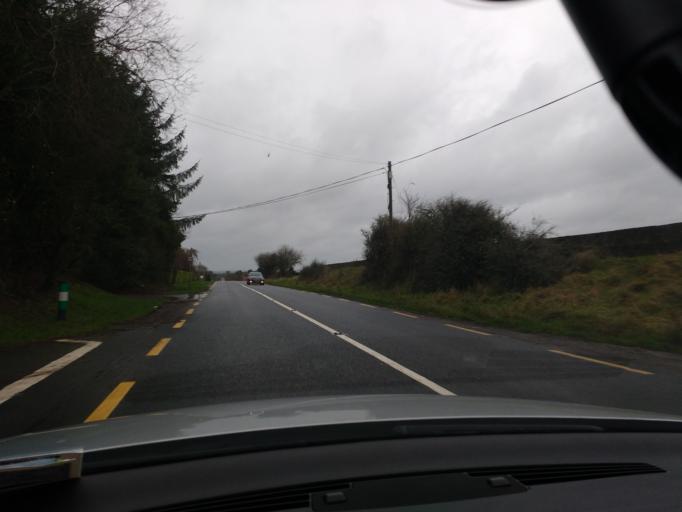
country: IE
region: Munster
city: Thurles
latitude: 52.6748
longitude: -7.7688
